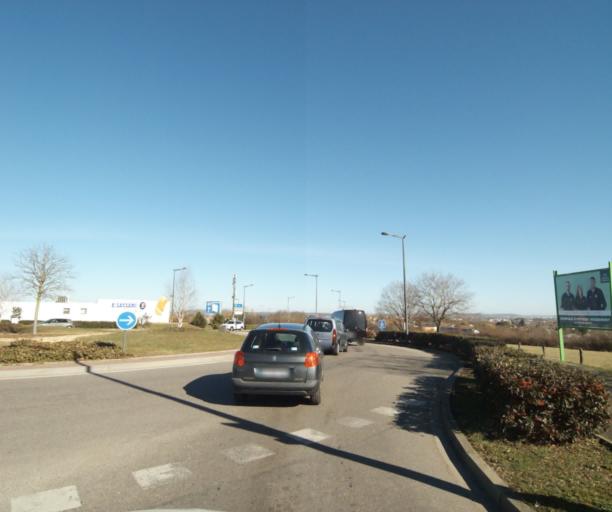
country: FR
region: Lorraine
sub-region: Departement de Meurthe-et-Moselle
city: Vandoeuvre-les-Nancy
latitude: 48.6517
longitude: 6.1792
